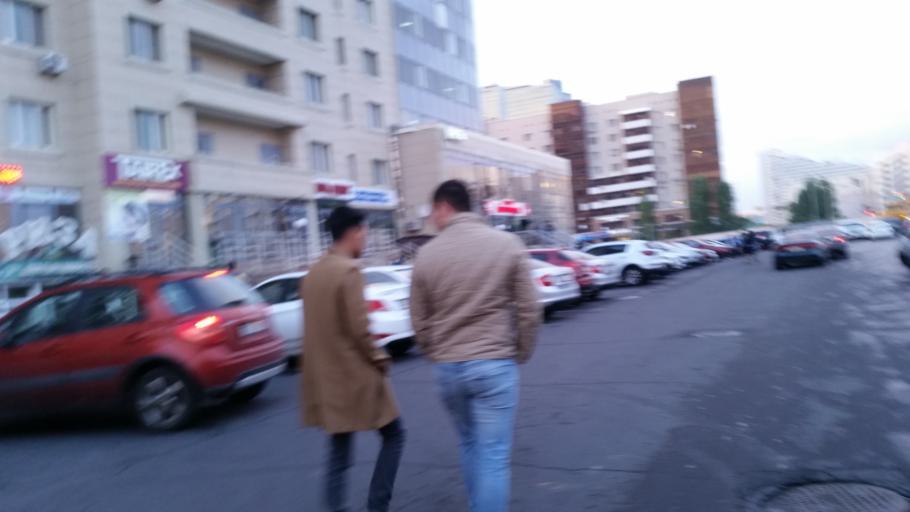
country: KZ
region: Astana Qalasy
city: Astana
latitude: 51.1232
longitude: 71.4220
